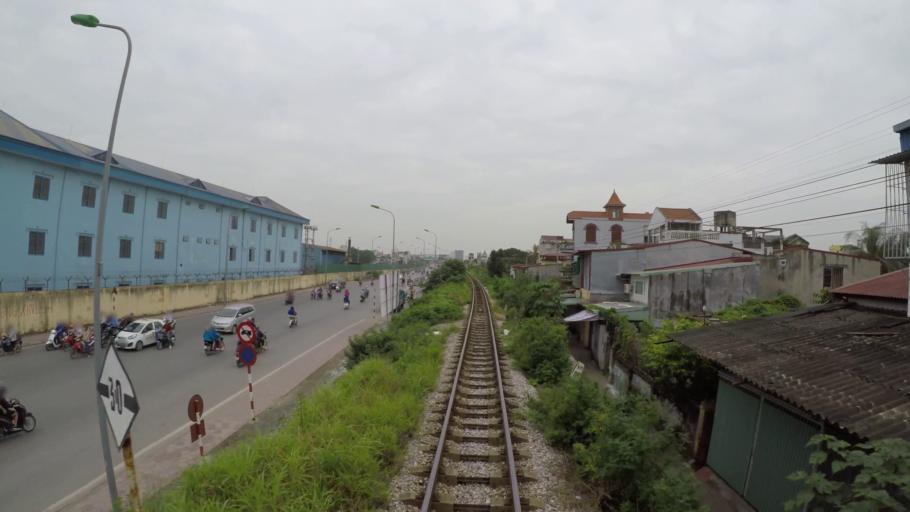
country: VN
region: Hai Phong
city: An Duong
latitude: 20.8723
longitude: 106.6474
